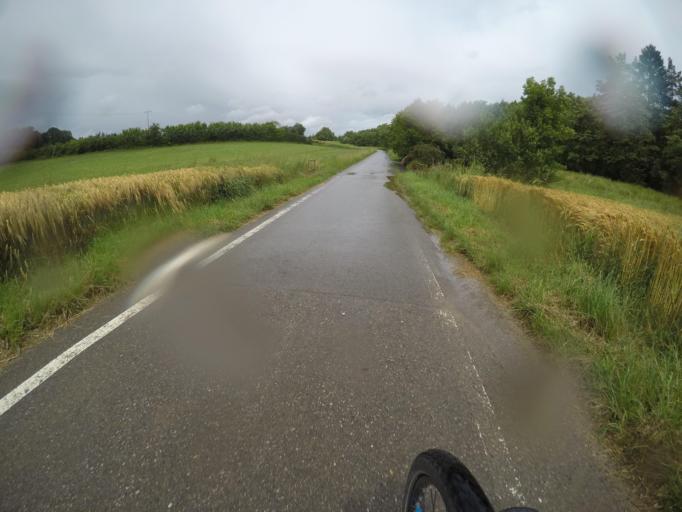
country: DE
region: Baden-Wuerttemberg
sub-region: Regierungsbezirk Stuttgart
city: Bondorf
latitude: 48.5392
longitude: 8.8221
